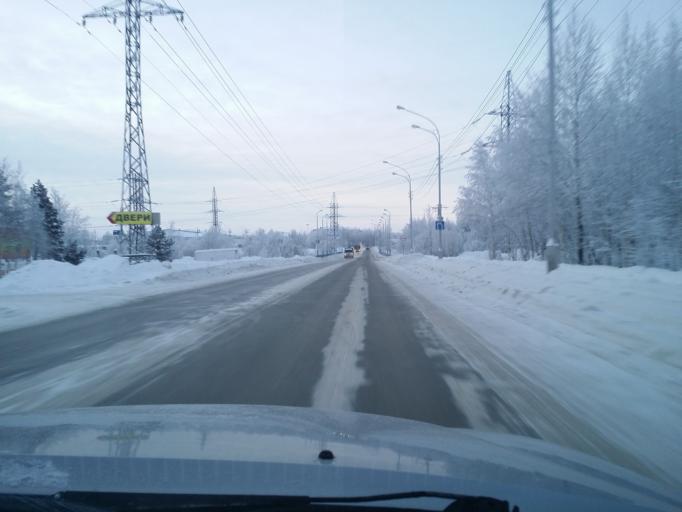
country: RU
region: Khanty-Mansiyskiy Avtonomnyy Okrug
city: Nizhnevartovsk
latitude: 60.9497
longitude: 76.5076
